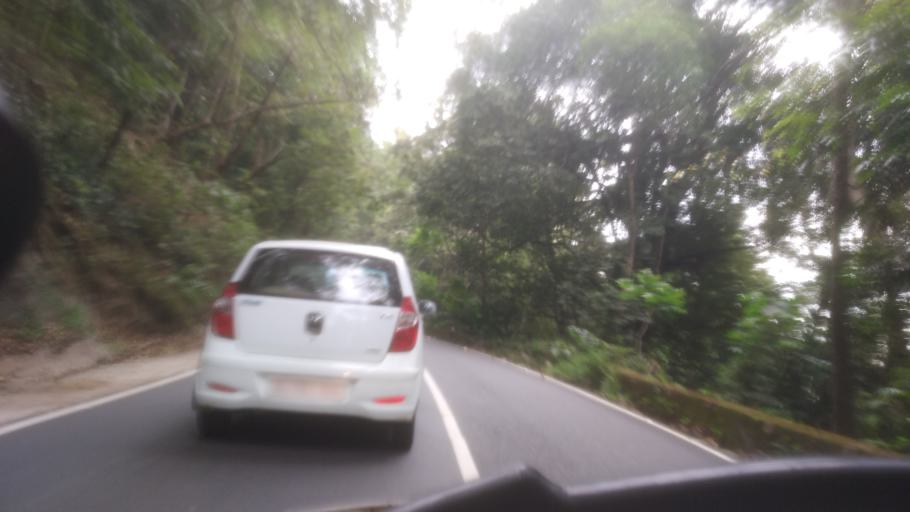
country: IN
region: Kerala
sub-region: Idukki
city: Kuttampuzha
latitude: 10.0582
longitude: 76.8109
